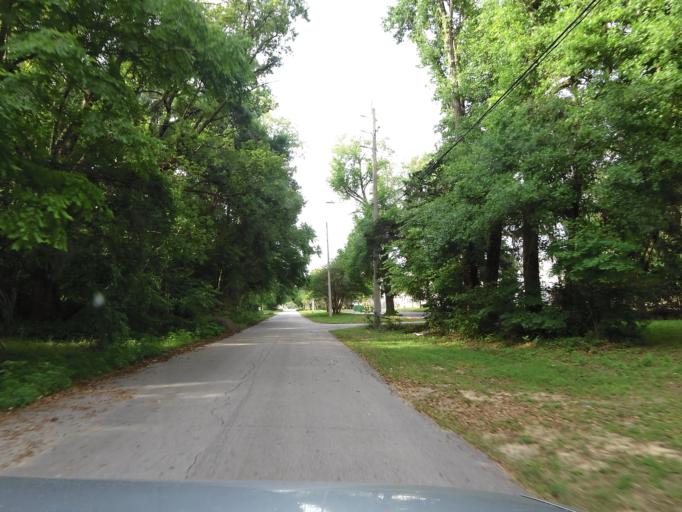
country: US
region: Florida
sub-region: Duval County
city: Jacksonville
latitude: 30.3307
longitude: -81.5978
